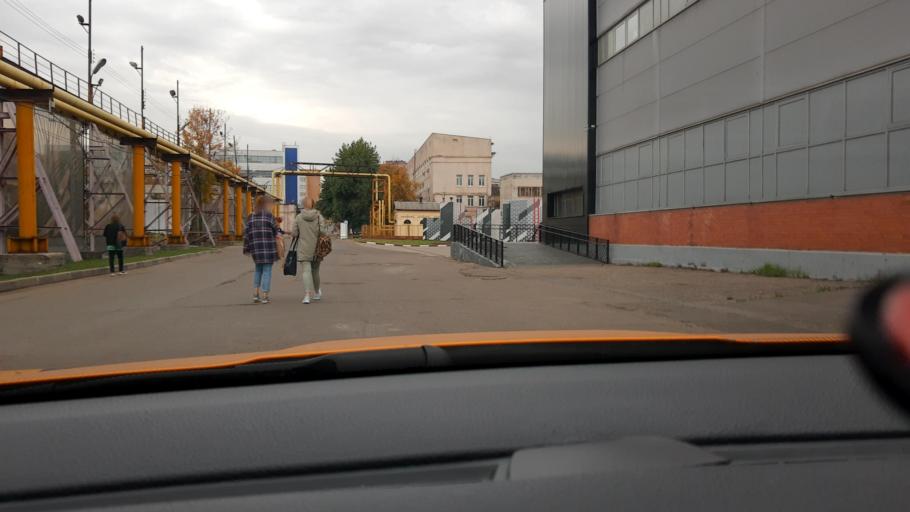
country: RU
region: Moscow
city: Taganskiy
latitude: 55.7202
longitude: 37.6841
